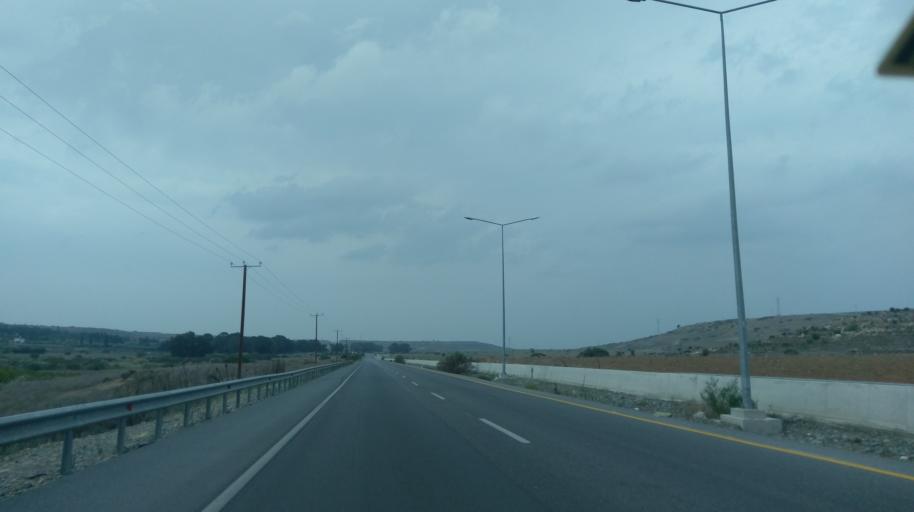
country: CY
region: Lefkosia
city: Akaki
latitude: 35.1953
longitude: 33.1053
